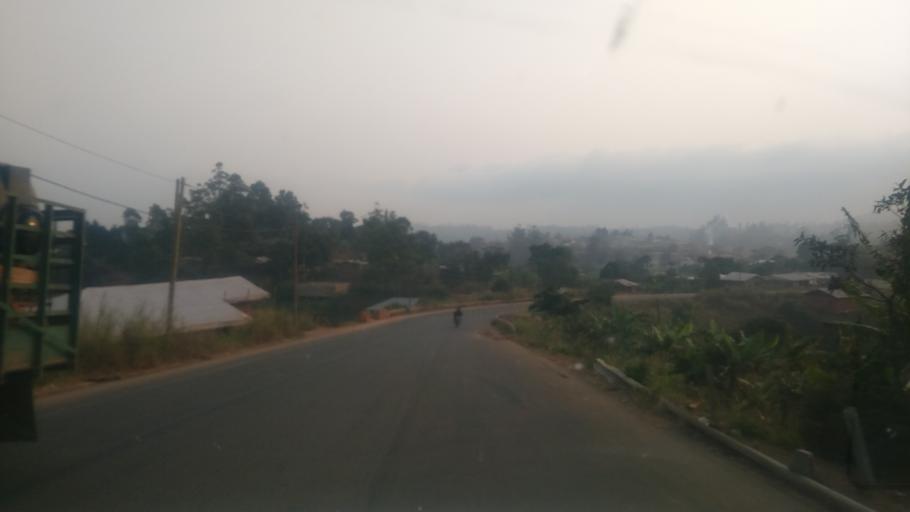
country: CM
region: West
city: Bana
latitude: 5.1401
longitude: 10.2951
